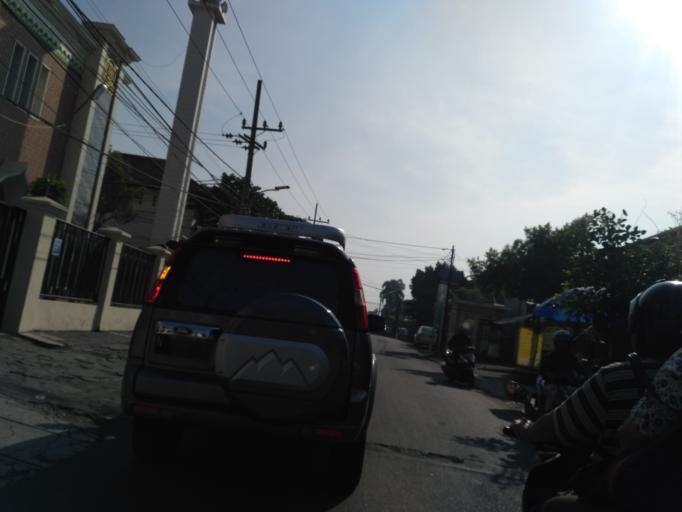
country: ID
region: East Java
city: Malang
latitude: -7.9497
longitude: 112.6234
